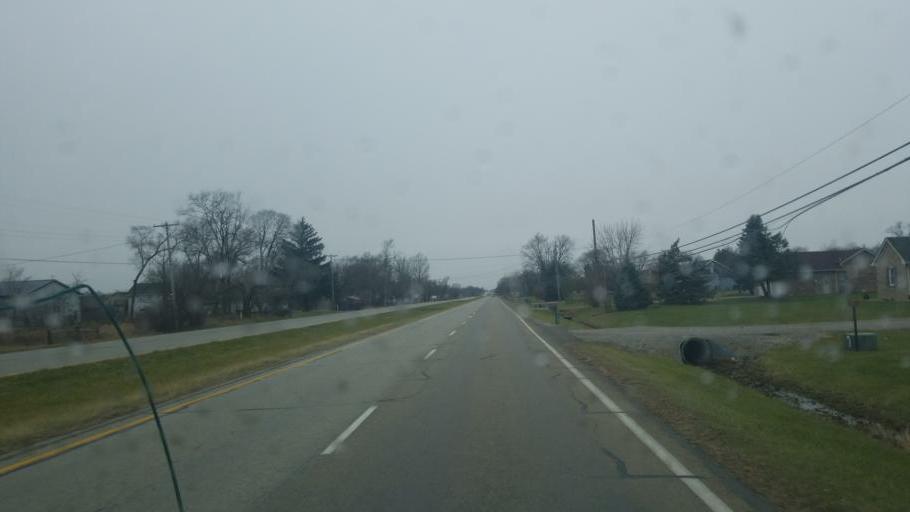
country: US
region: Indiana
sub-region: Hancock County
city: Greenfield
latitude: 39.7884
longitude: -85.7002
